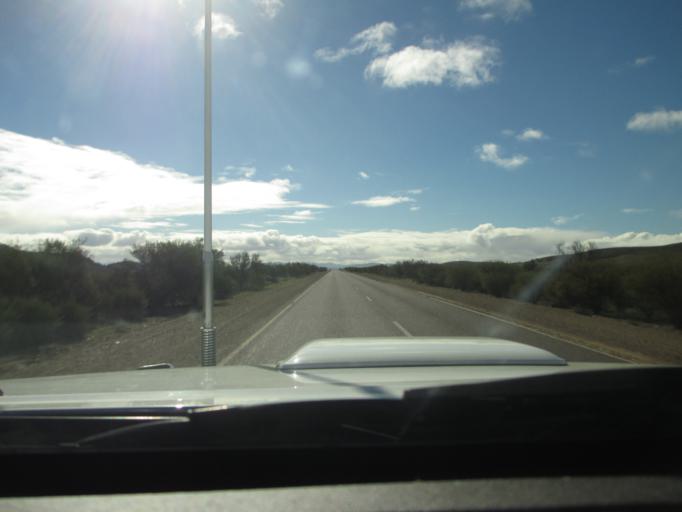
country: AU
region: South Australia
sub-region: Flinders Ranges
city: Quorn
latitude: -31.9313
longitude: 138.4161
